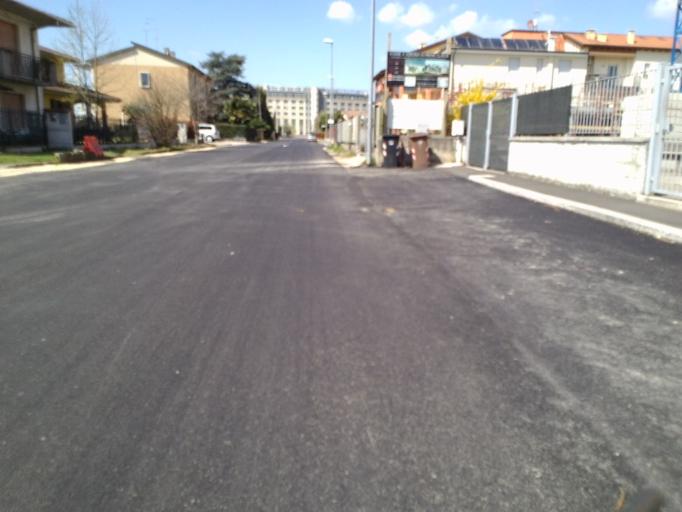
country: IT
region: Veneto
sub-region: Provincia di Verona
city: Dossobuono
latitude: 45.4067
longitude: 10.9283
